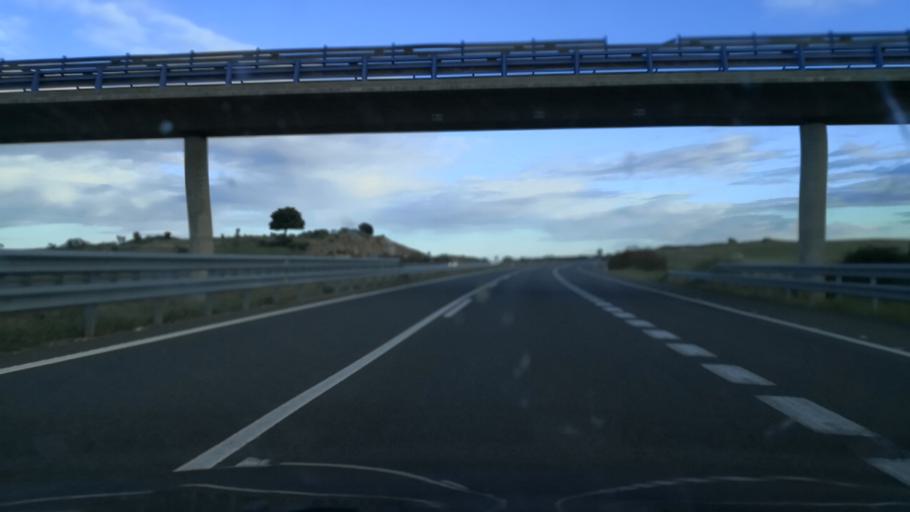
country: ES
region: Extremadura
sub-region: Provincia de Caceres
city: Caceres
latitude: 39.4677
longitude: -6.4235
